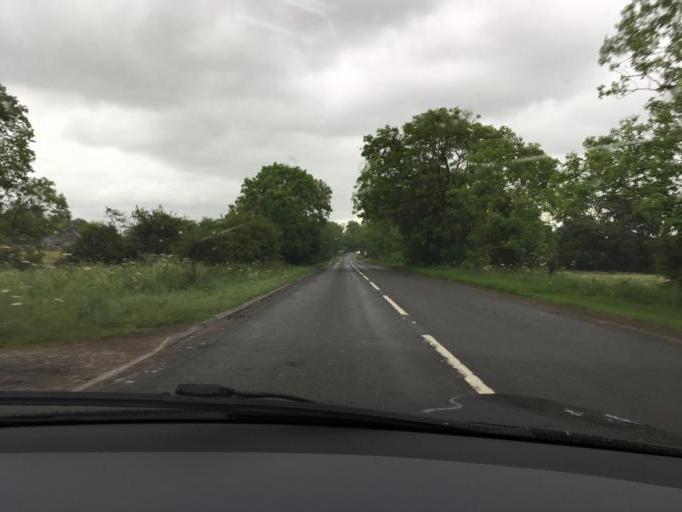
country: GB
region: England
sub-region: Staffordshire
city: Mayfield
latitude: 53.0344
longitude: -1.8135
